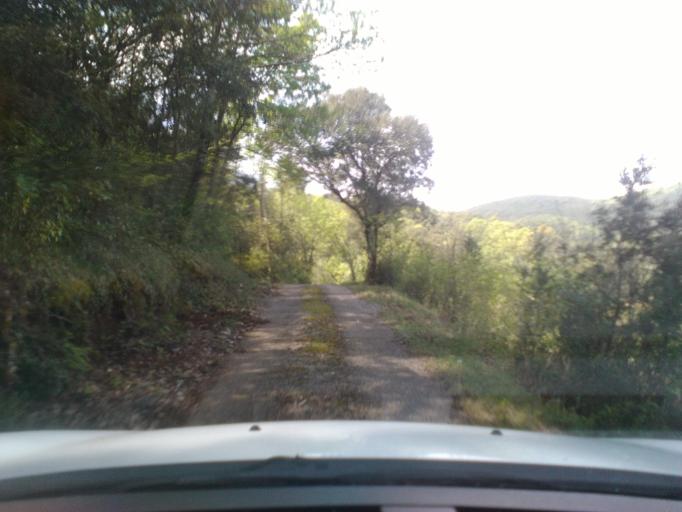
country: FR
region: Languedoc-Roussillon
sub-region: Departement du Gard
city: Saint-Hippolyte-du-Fort
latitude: 43.9922
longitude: 3.8831
